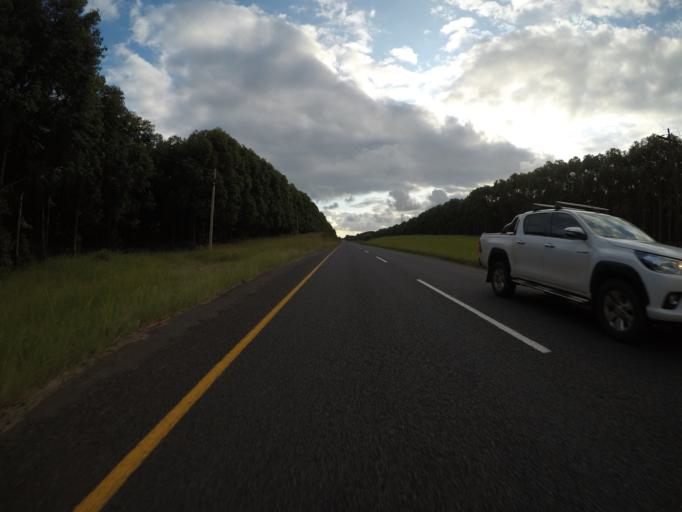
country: ZA
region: KwaZulu-Natal
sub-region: uMkhanyakude District Municipality
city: Mtubatuba
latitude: -28.3911
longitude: 32.2267
